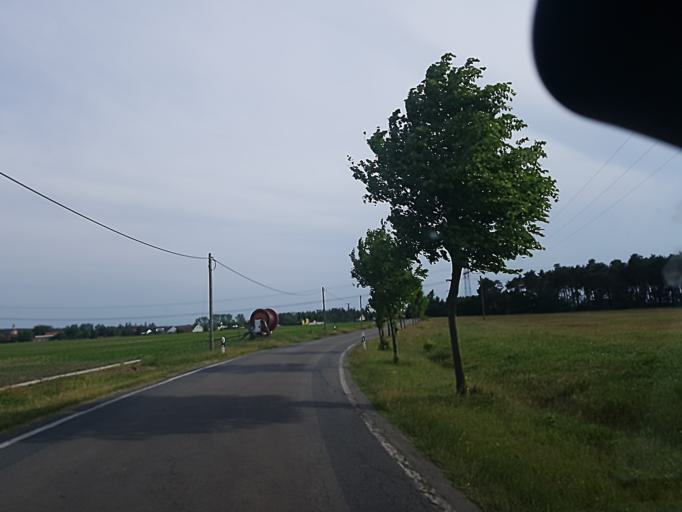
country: DE
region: Saxony-Anhalt
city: Jessen
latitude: 51.8277
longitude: 12.9479
